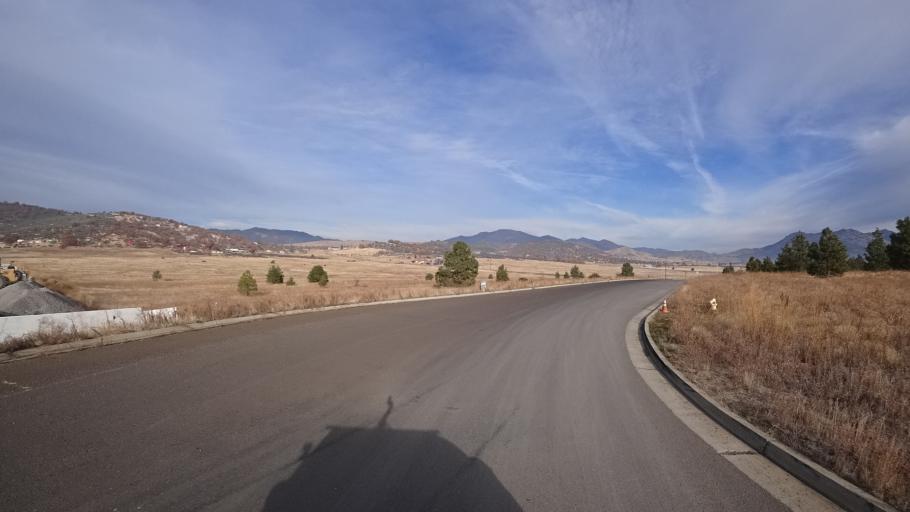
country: US
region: California
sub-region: Siskiyou County
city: Yreka
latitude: 41.7337
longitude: -122.5972
